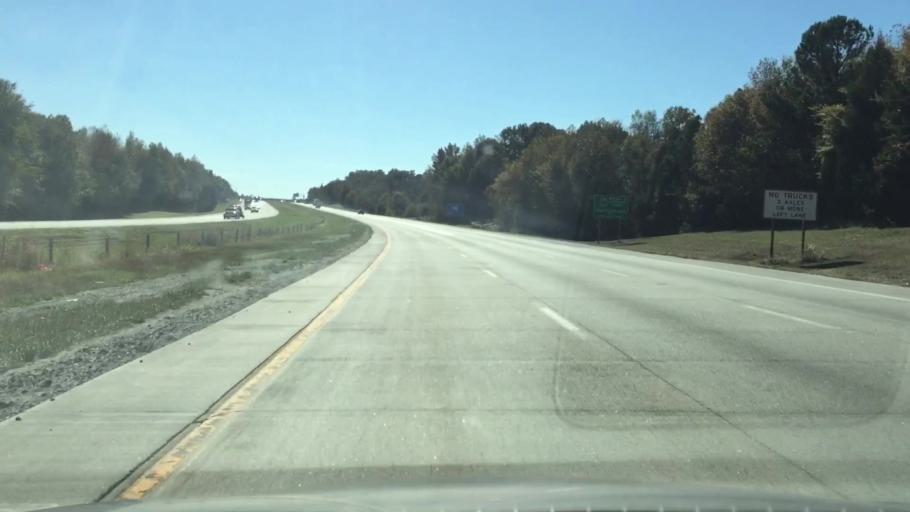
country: US
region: North Carolina
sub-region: Randolph County
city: Archdale
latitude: 35.9146
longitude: -79.9478
